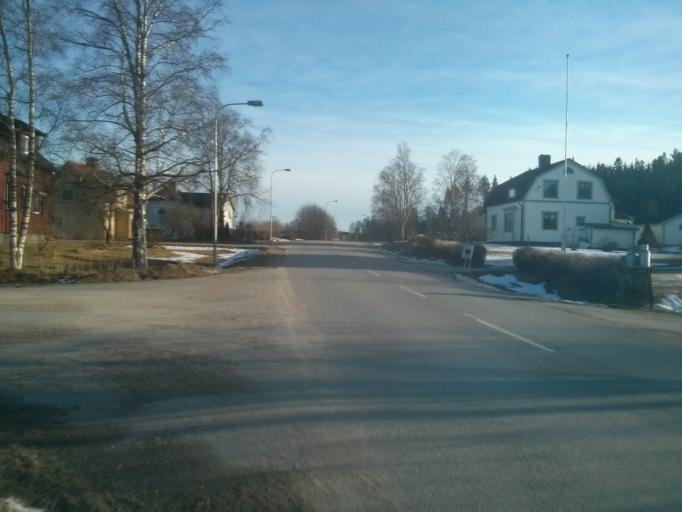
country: SE
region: Vaesternorrland
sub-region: Sundsvalls Kommun
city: Njurundabommen
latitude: 62.2601
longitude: 17.3781
